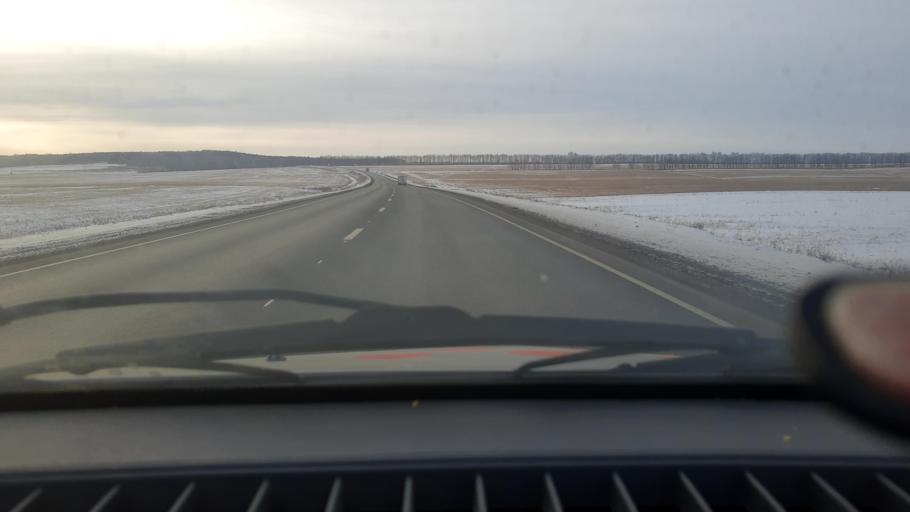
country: RU
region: Bashkortostan
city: Mikhaylovka
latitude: 54.8666
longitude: 55.7057
